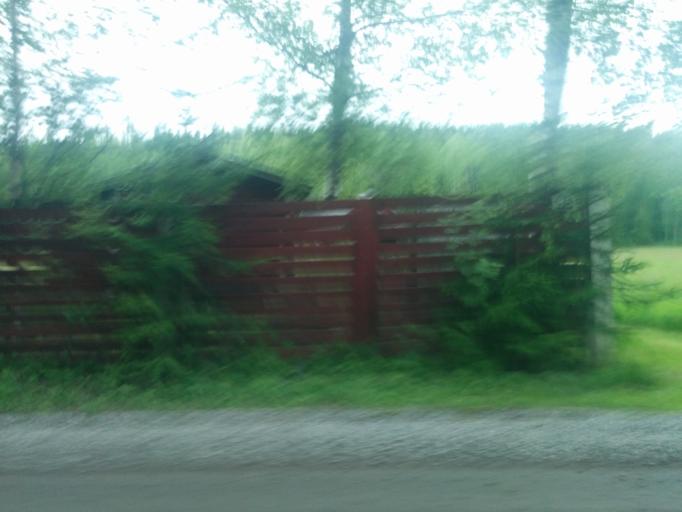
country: FI
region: Pirkanmaa
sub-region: Tampere
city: Kuhmalahti
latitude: 61.6996
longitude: 24.5620
